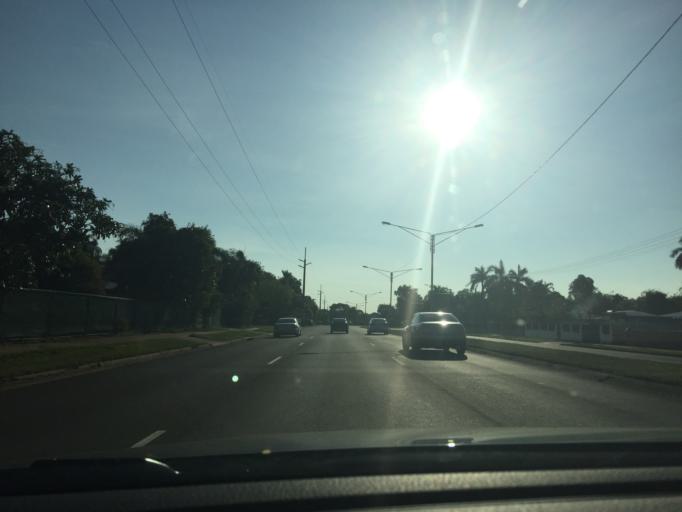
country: AU
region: Northern Territory
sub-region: Darwin
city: Nightcliff
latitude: -12.3831
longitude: 130.8743
